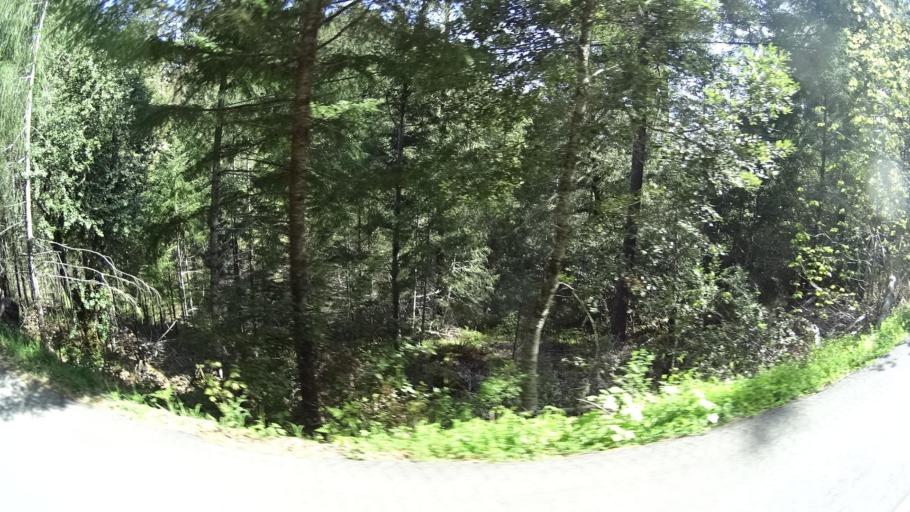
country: US
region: California
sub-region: Humboldt County
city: Redway
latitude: 40.0764
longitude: -123.6546
